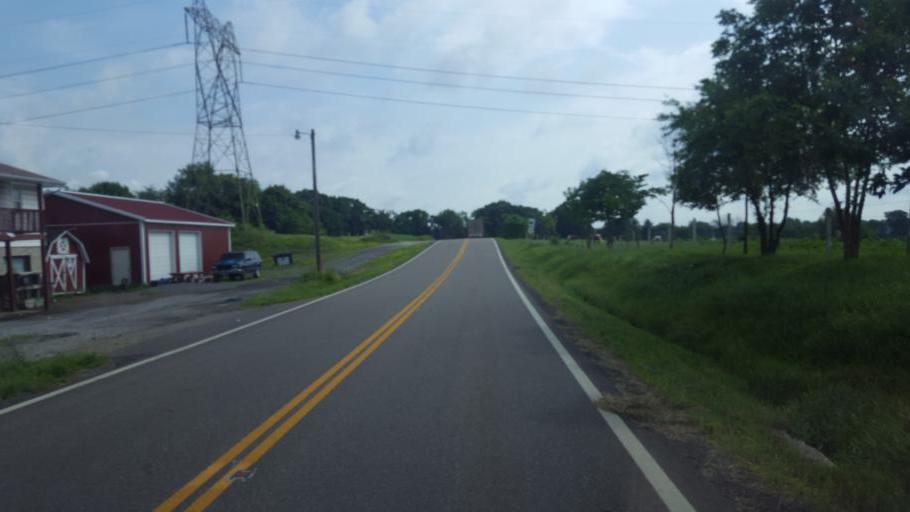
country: US
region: Ohio
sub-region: Columbiana County
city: Salineville
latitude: 40.5965
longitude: -80.8435
